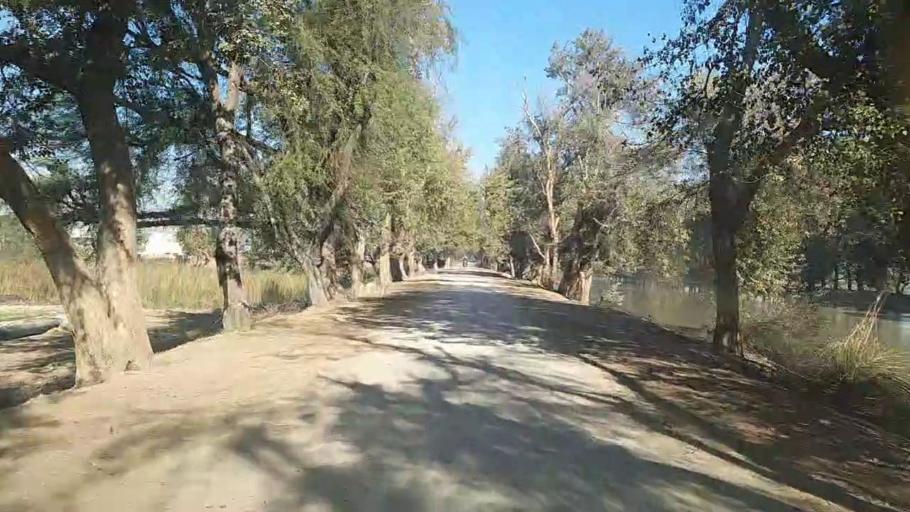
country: PK
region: Sindh
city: Khairpur
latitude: 28.0047
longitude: 69.6514
